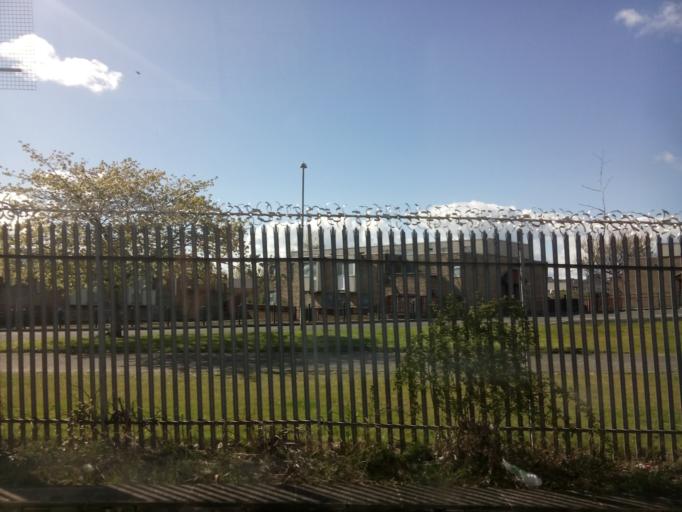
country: GB
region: England
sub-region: Newcastle upon Tyne
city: Newcastle upon Tyne
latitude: 54.9591
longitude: -1.6168
